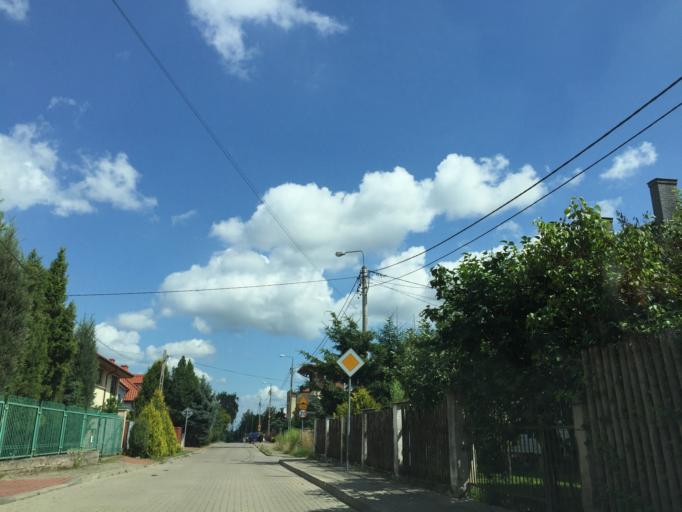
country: PL
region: Podlasie
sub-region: Bialystok
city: Bialystok
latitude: 53.1144
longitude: 23.1712
